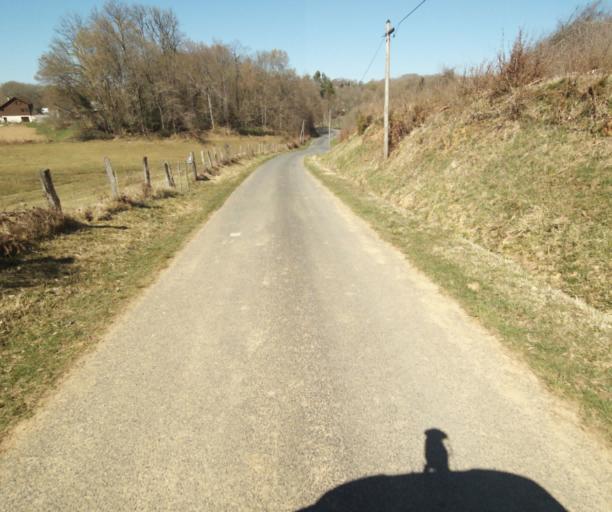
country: FR
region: Limousin
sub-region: Departement de la Correze
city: Saint-Clement
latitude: 45.3166
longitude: 1.6964
